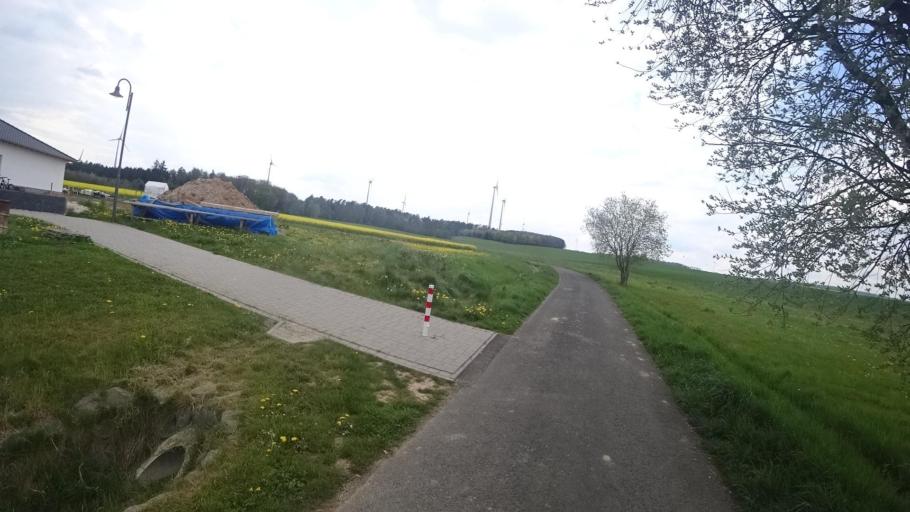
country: DE
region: Rheinland-Pfalz
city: Niederkumbd
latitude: 50.0142
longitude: 7.5330
